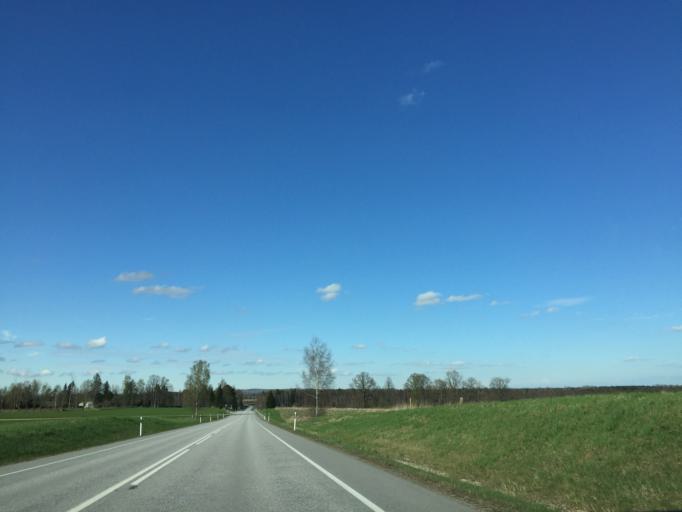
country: EE
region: Vorumaa
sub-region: Antsla vald
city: Vana-Antsla
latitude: 57.8816
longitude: 26.2817
